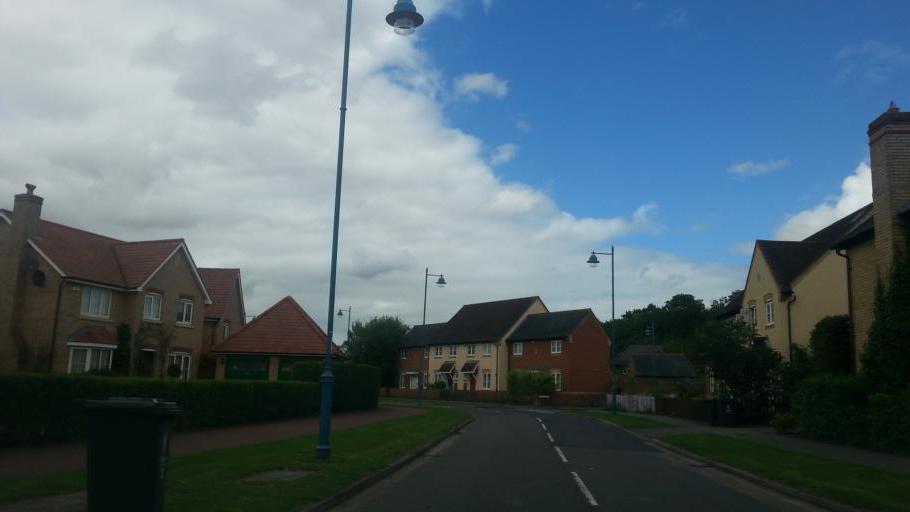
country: GB
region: England
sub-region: Cambridgeshire
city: Papworth Everard
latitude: 52.2163
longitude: -0.0689
